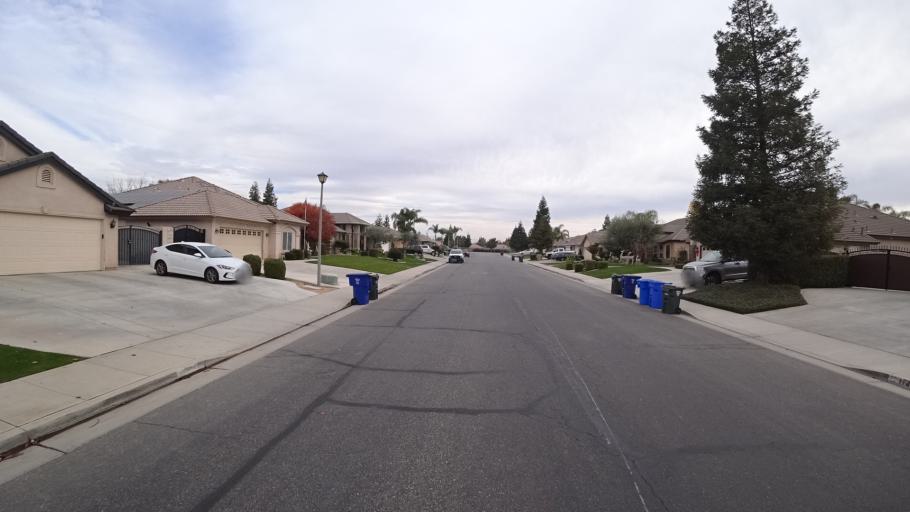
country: US
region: California
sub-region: Kern County
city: Rosedale
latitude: 35.4174
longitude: -119.1296
